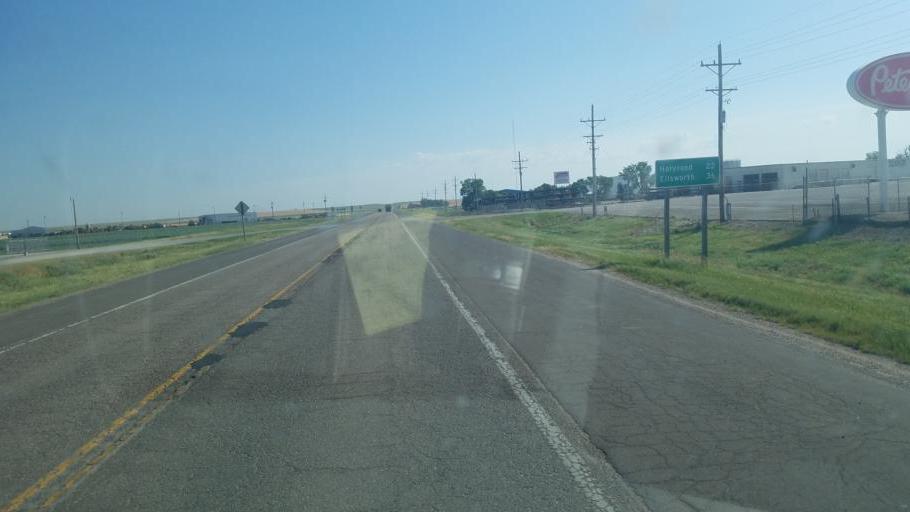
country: US
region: Kansas
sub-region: Barton County
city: Great Bend
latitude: 38.3663
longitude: -98.6948
